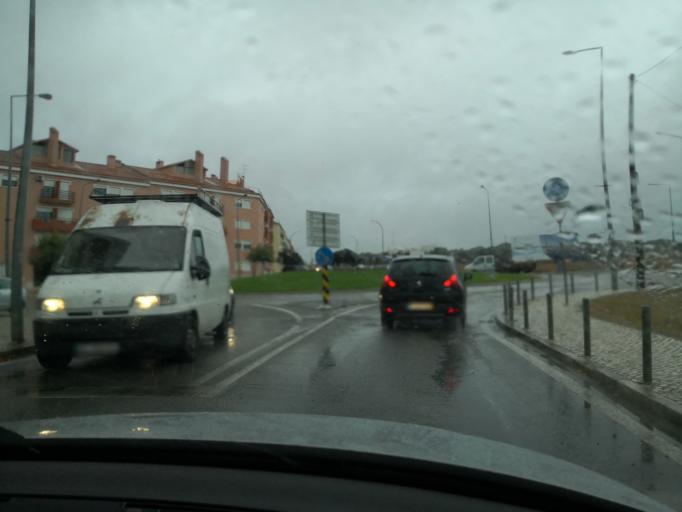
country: PT
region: Setubal
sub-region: Moita
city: Moita
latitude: 38.6472
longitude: -8.9867
